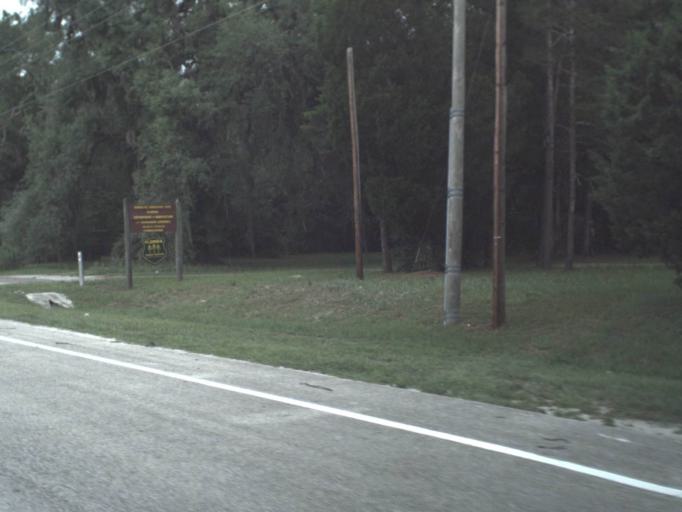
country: US
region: Florida
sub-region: Alachua County
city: Waldo
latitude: 29.8458
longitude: -82.1595
